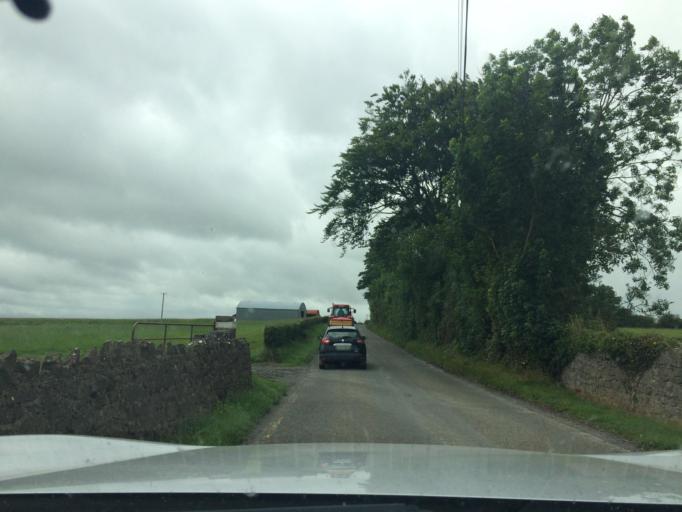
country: IE
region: Munster
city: Thurles
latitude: 52.6275
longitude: -7.8739
